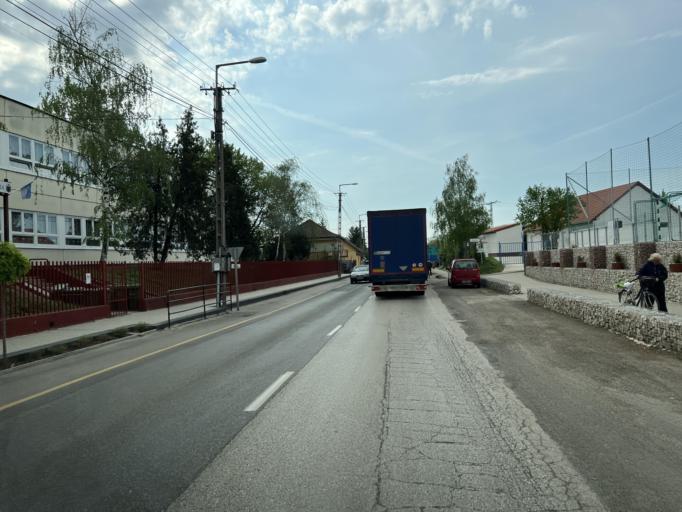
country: HU
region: Pest
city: Farmos
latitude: 47.3609
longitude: 19.8475
